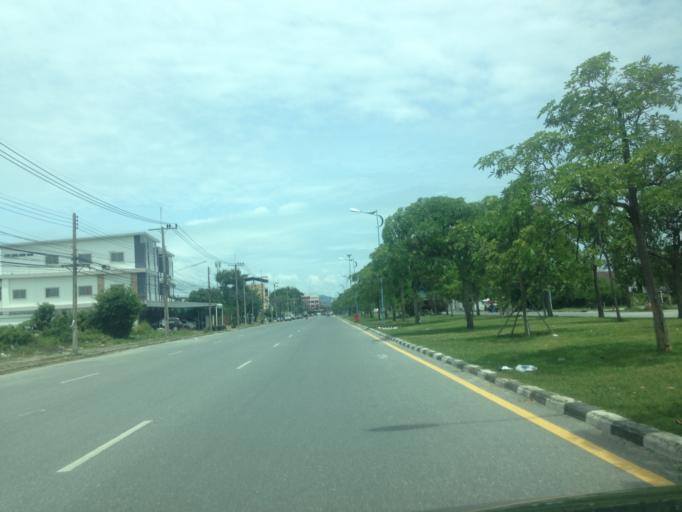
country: TH
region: Chon Buri
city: Chon Buri
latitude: 13.3422
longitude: 100.9501
